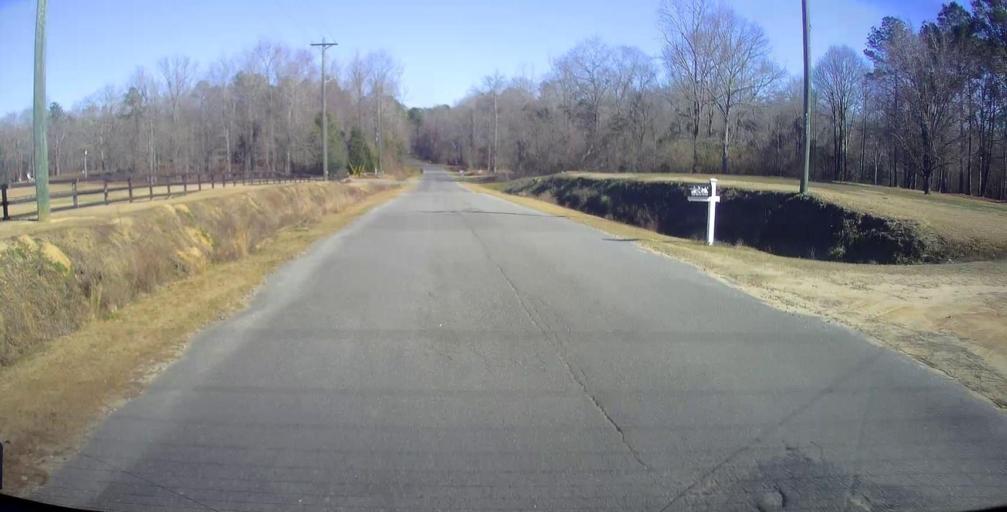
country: US
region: Georgia
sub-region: Crawford County
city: Knoxville
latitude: 32.7155
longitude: -84.0042
